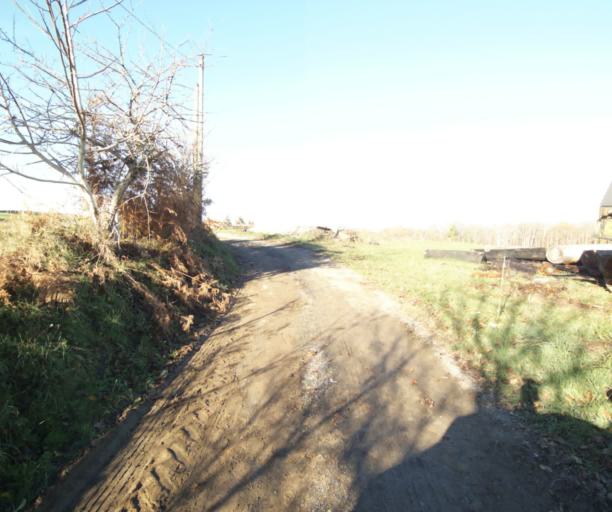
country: FR
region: Limousin
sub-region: Departement de la Correze
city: Sainte-Fortunade
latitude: 45.2108
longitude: 1.7988
